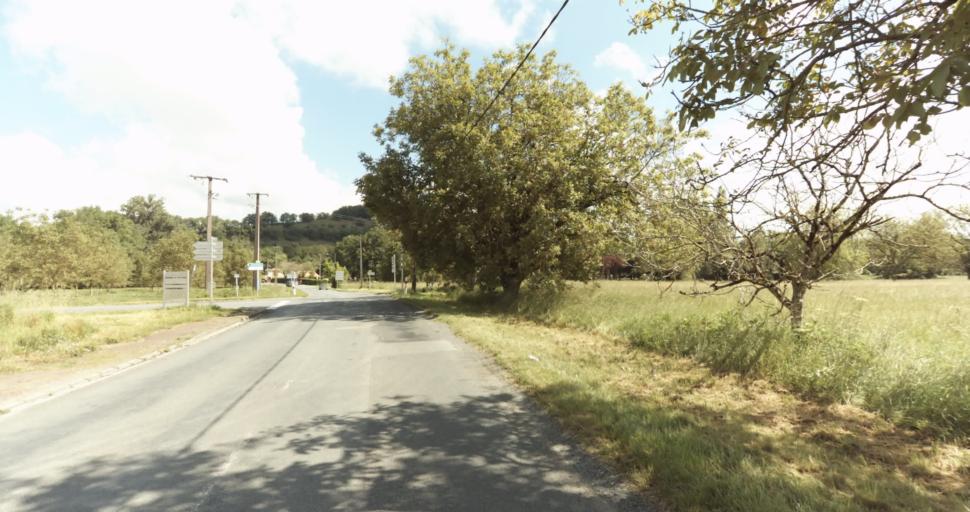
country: FR
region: Aquitaine
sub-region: Departement de la Dordogne
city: Le Bugue
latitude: 44.8516
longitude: 0.9105
